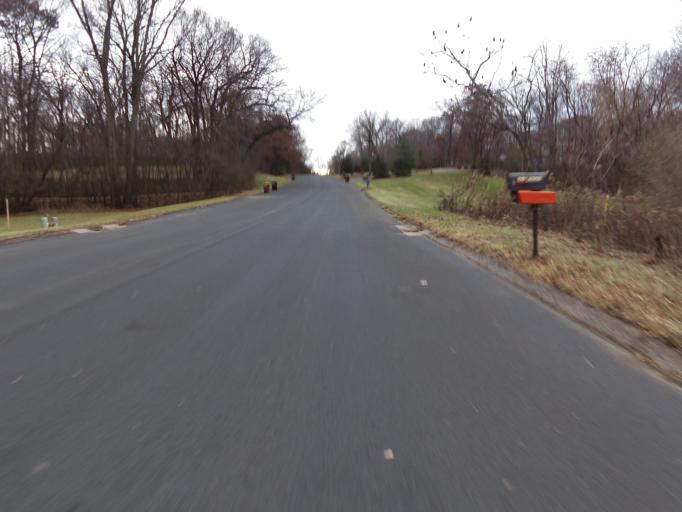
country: US
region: Minnesota
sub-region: Washington County
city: Lake Elmo
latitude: 44.9822
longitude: -92.8698
